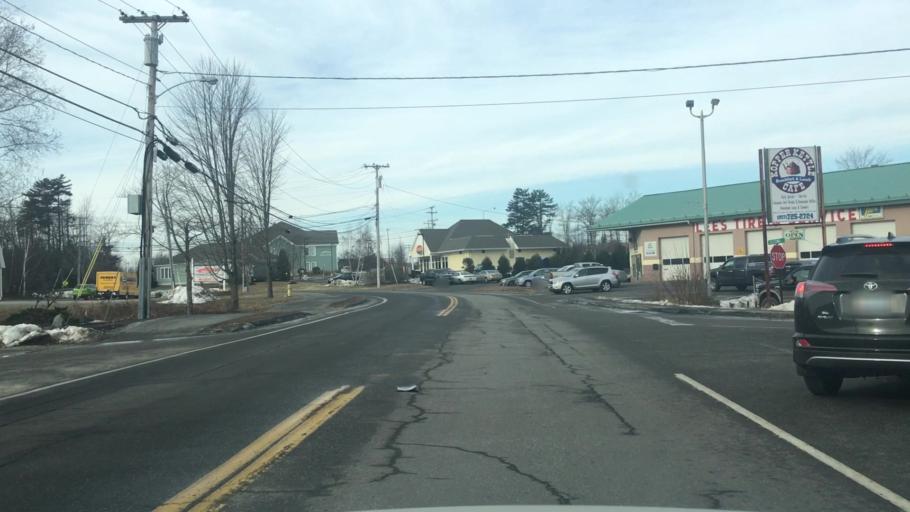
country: US
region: Maine
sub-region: Sagadahoc County
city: Topsham
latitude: 43.9362
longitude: -69.9678
